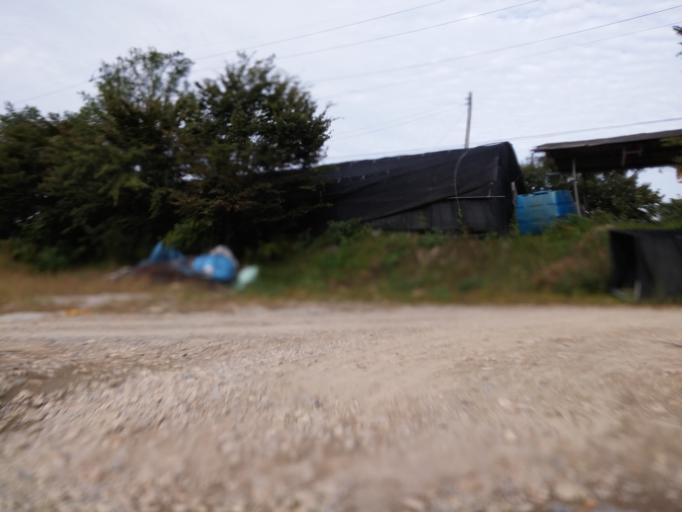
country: KR
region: Chungcheongnam-do
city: Yonmu
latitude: 36.1566
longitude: 127.2031
